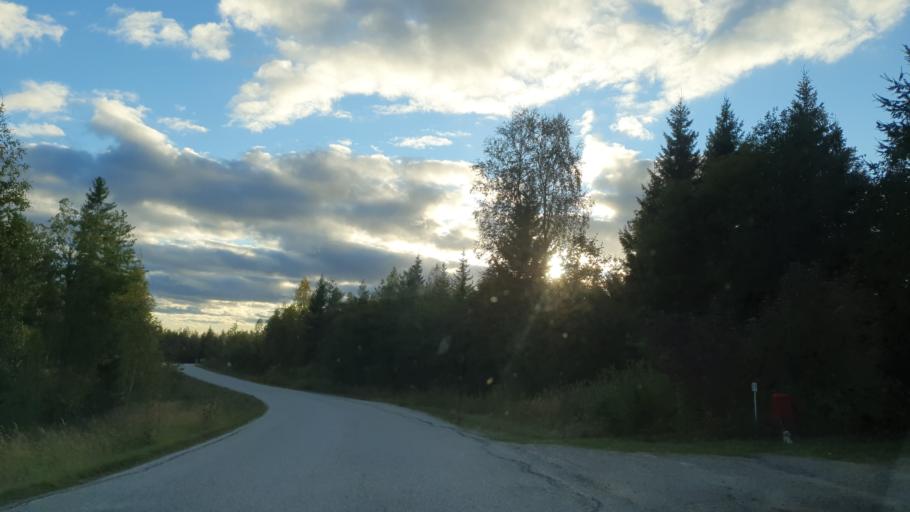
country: FI
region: Kainuu
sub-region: Kehys-Kainuu
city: Kuhmo
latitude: 63.9550
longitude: 29.7249
